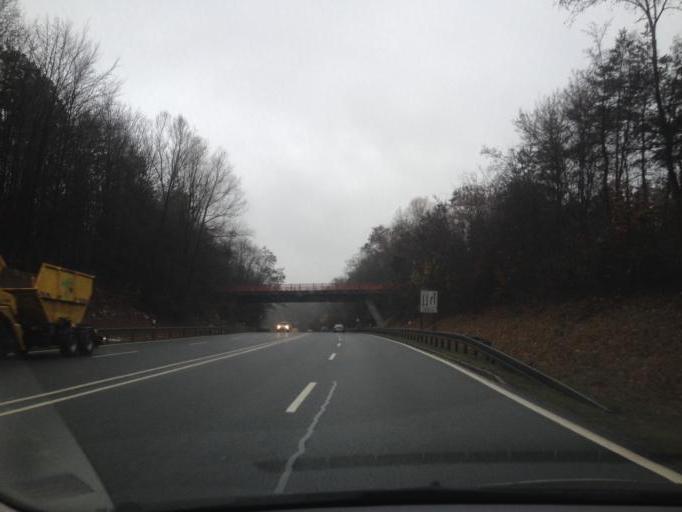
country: DE
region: Bavaria
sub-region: Regierungsbezirk Mittelfranken
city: Heroldsberg
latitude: 49.5124
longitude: 11.1358
